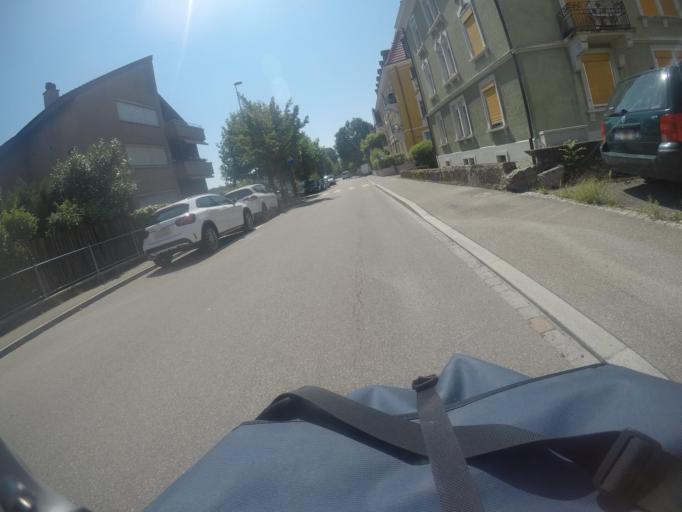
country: CH
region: Thurgau
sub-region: Arbon District
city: Arbon
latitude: 47.5077
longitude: 9.4281
